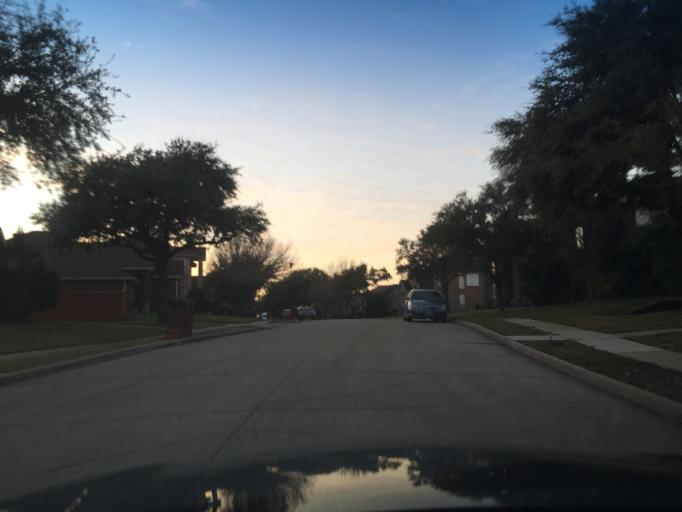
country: US
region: Texas
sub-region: Dallas County
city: Carrollton
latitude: 32.9861
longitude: -96.8945
